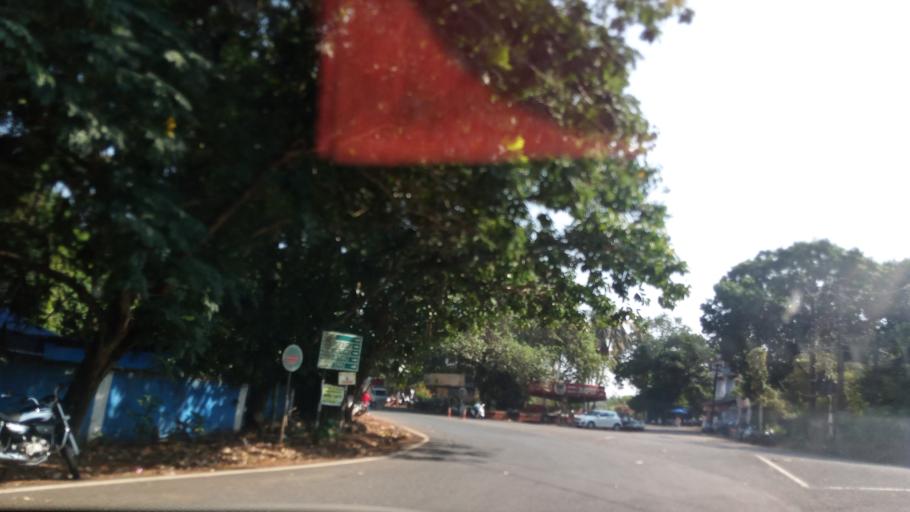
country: IN
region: Goa
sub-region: North Goa
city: Bandora
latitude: 15.4135
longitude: 73.9886
